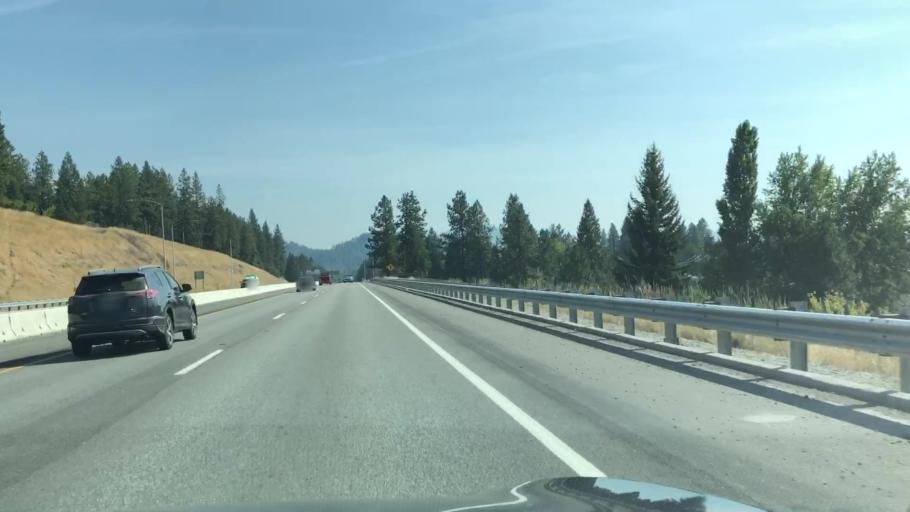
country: US
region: Idaho
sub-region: Kootenai County
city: Coeur d'Alene
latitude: 47.6876
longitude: -116.7639
